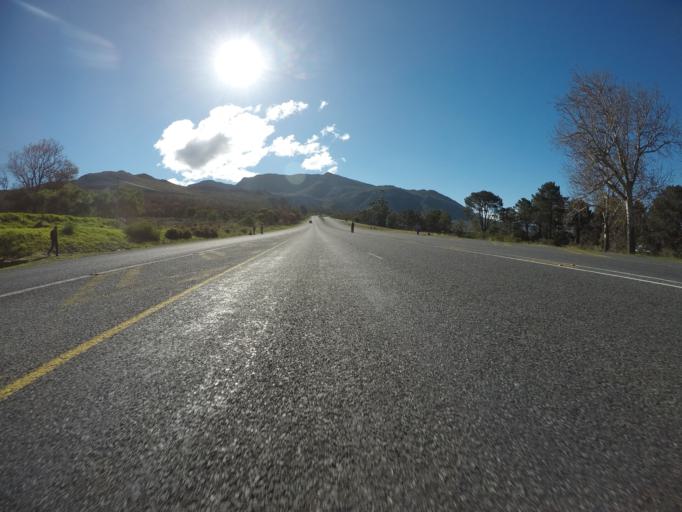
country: ZA
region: Western Cape
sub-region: Overberg District Municipality
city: Grabouw
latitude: -34.2279
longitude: 19.1877
